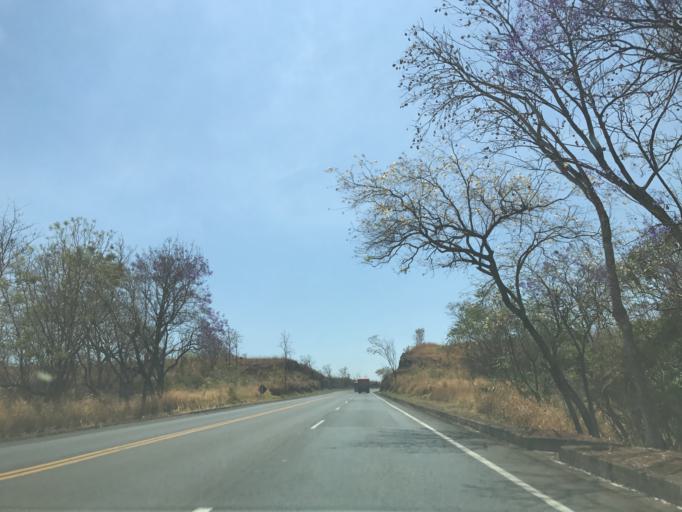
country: BR
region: Minas Gerais
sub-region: Frutal
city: Frutal
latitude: -19.8713
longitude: -48.9733
